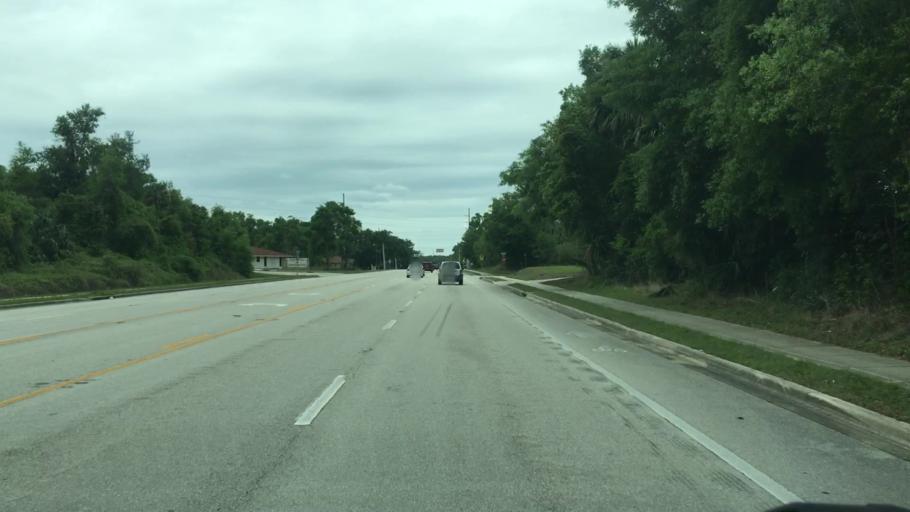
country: US
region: Florida
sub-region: Volusia County
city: De Land Southwest
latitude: 29.0037
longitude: -81.3158
